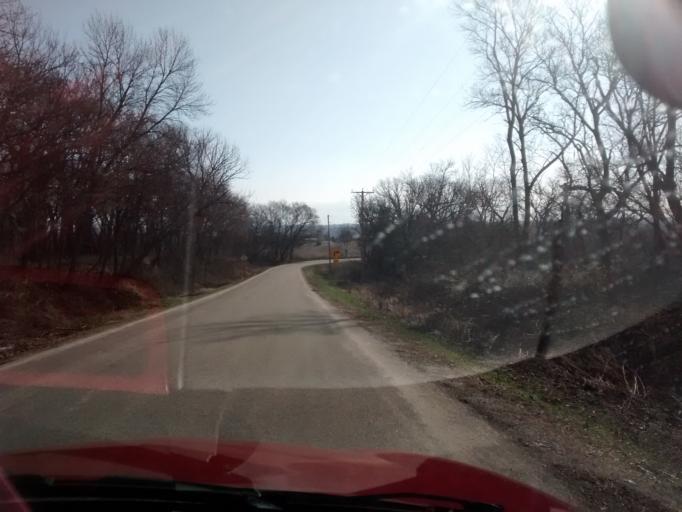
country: US
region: Iowa
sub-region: Pottawattamie County
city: Carter Lake
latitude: 41.4169
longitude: -95.8524
